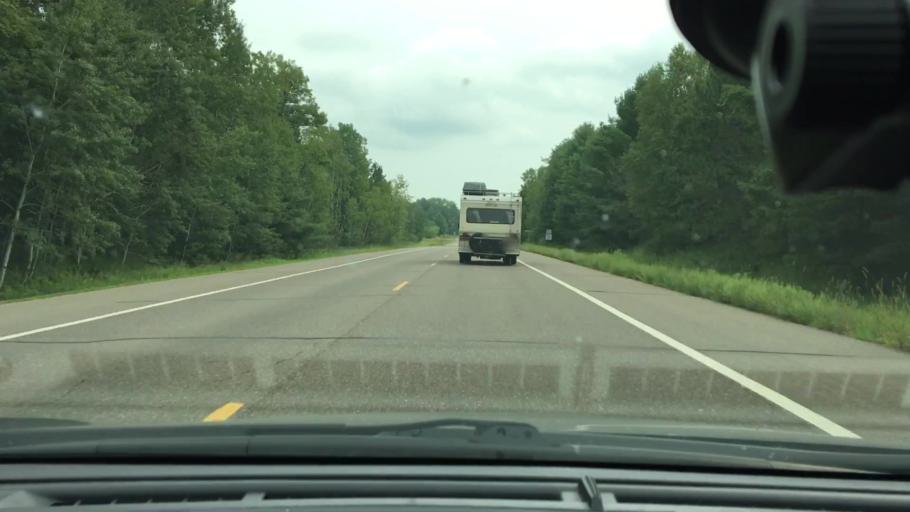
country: US
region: Minnesota
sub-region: Crow Wing County
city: Crosby
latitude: 46.4104
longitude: -93.8514
